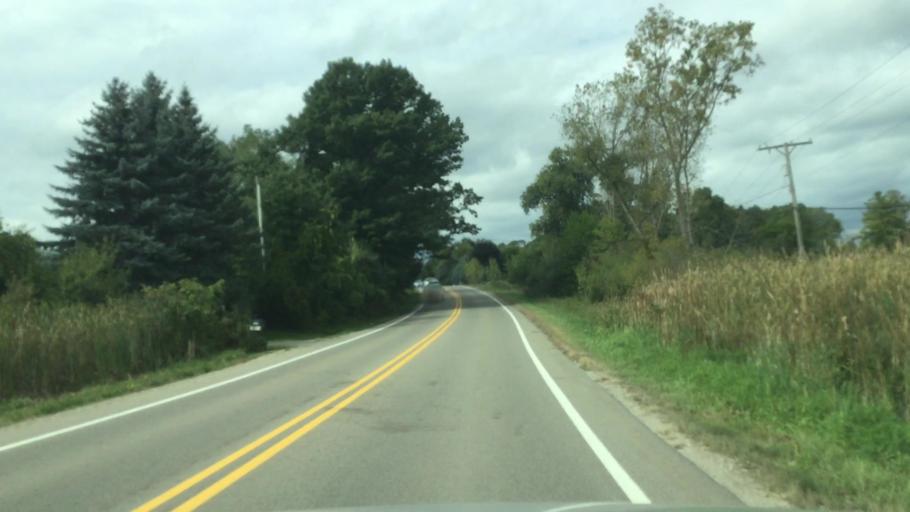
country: US
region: Michigan
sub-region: Livingston County
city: Brighton
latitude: 42.5495
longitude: -83.7806
